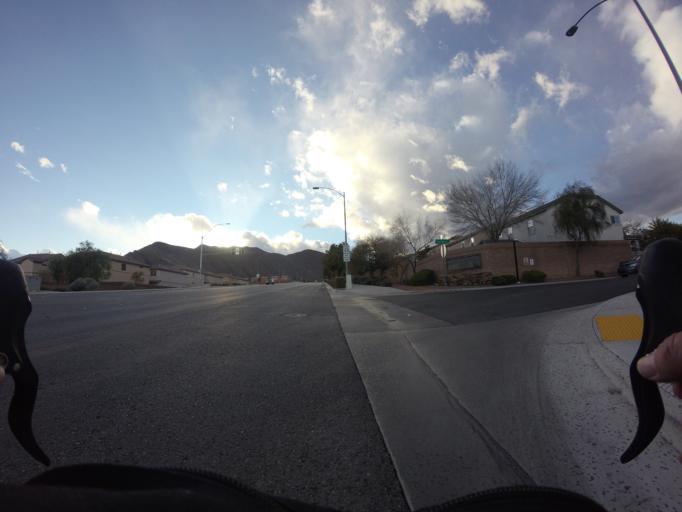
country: US
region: Nevada
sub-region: Clark County
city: Summerlin South
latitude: 36.2329
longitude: -115.3229
